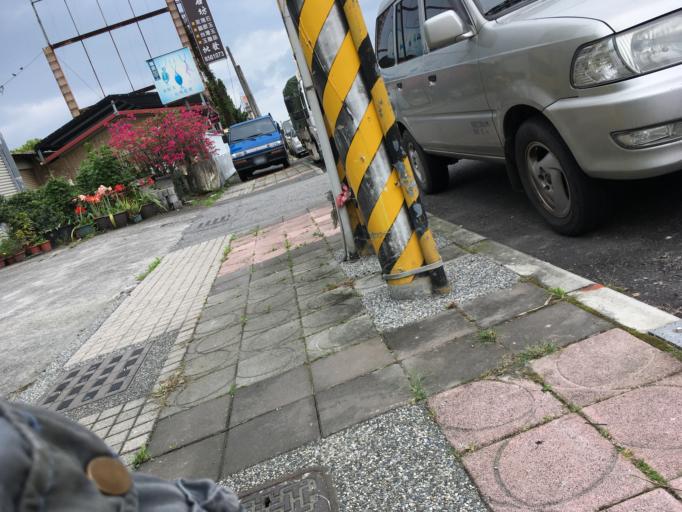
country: TW
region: Taiwan
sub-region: Hualien
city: Hualian
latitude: 23.9976
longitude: 121.5958
